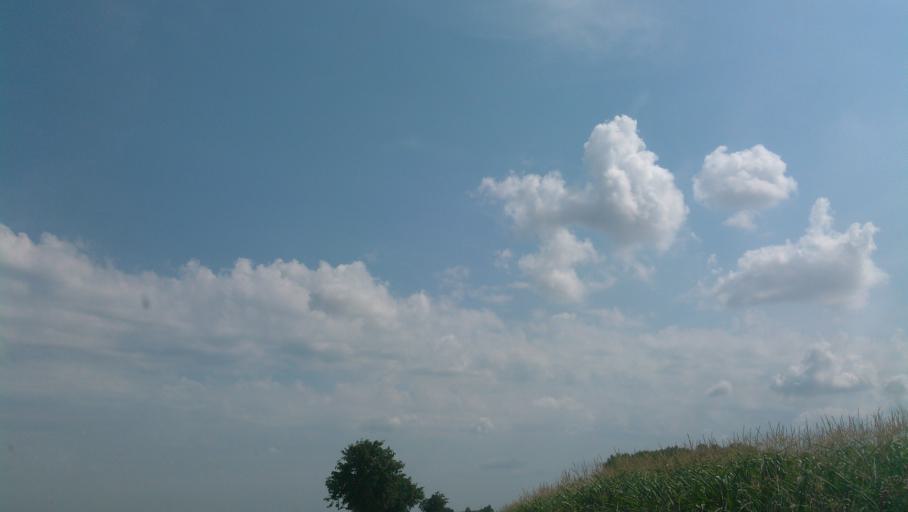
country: SK
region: Nitriansky
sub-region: Okres Nitra
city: Nitra
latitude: 48.4067
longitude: 18.0258
